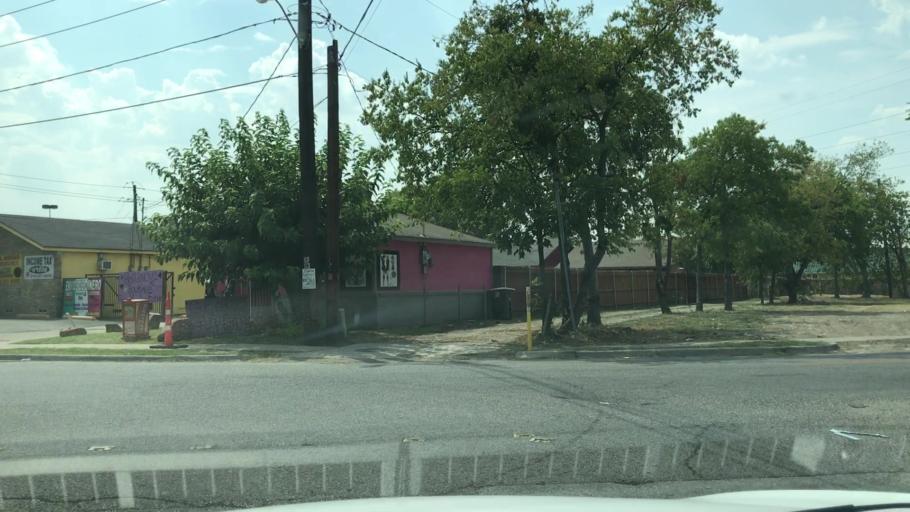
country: US
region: Texas
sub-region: Dallas County
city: University Park
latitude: 32.8653
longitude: -96.8619
